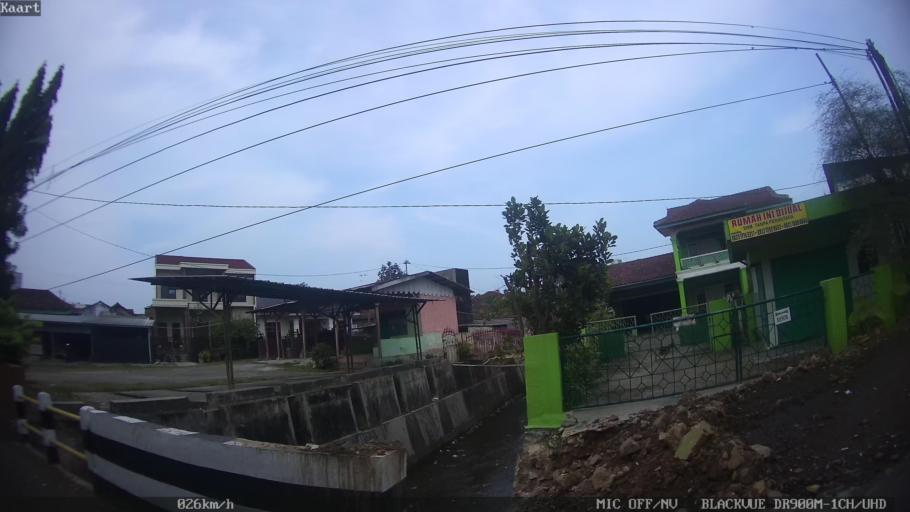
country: ID
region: Lampung
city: Bandarlampung
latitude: -5.4193
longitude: 105.2696
